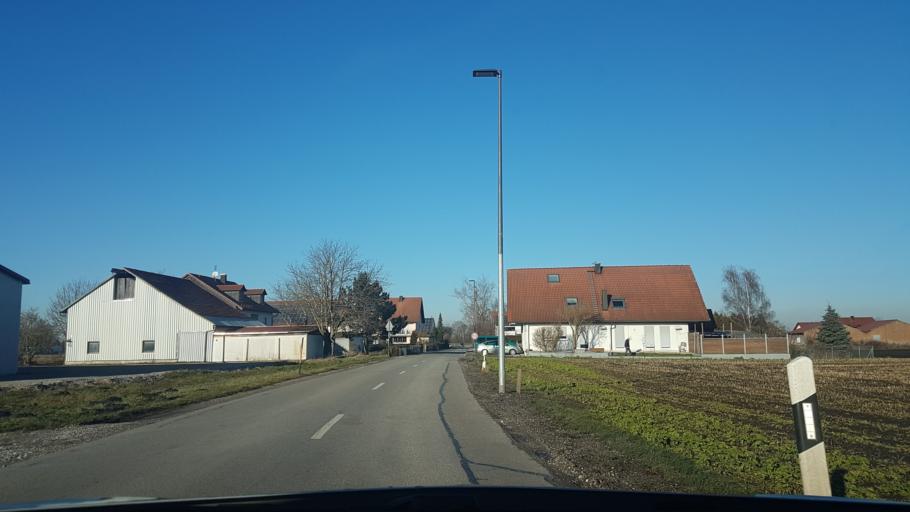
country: DE
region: Bavaria
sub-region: Upper Bavaria
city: Hallbergmoos
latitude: 48.2998
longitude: 11.7505
